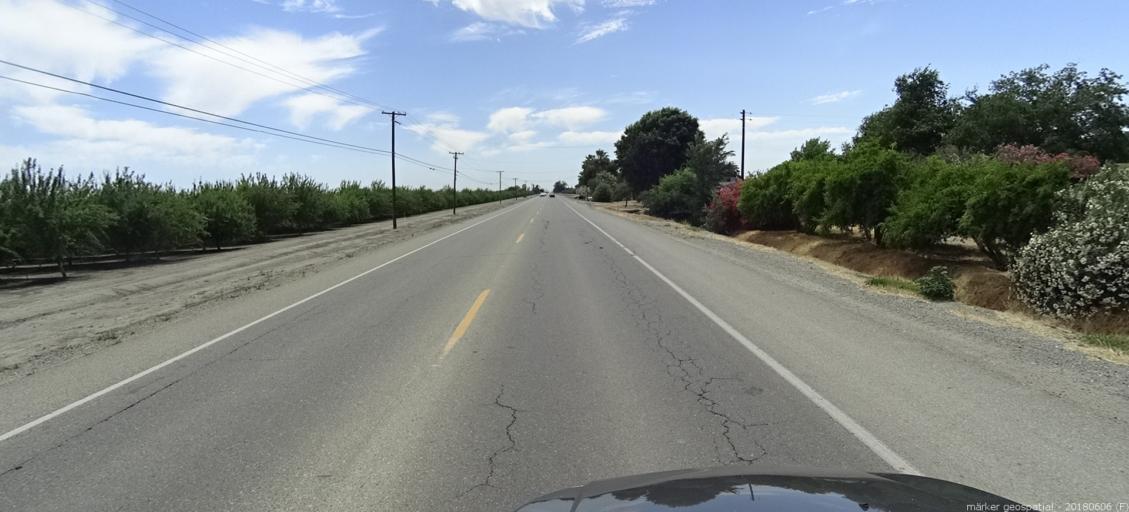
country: US
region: California
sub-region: Fresno County
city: Firebaugh
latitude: 36.8584
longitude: -120.4206
